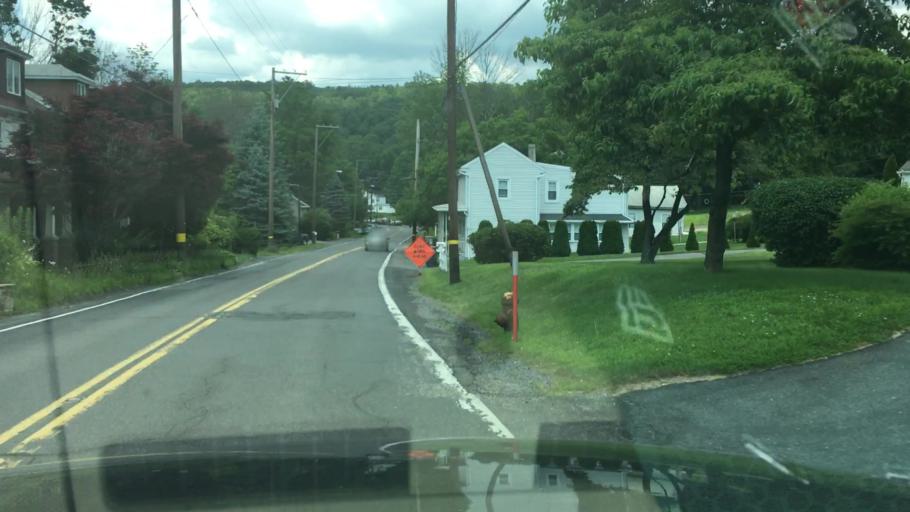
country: US
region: Pennsylvania
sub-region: Schuylkill County
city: Minersville
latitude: 40.6971
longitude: -76.2840
